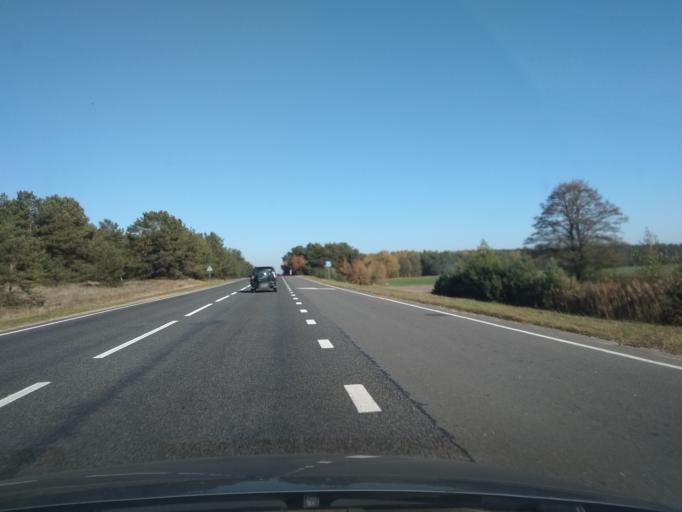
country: BY
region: Brest
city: Kobryn
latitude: 52.1310
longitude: 24.3056
